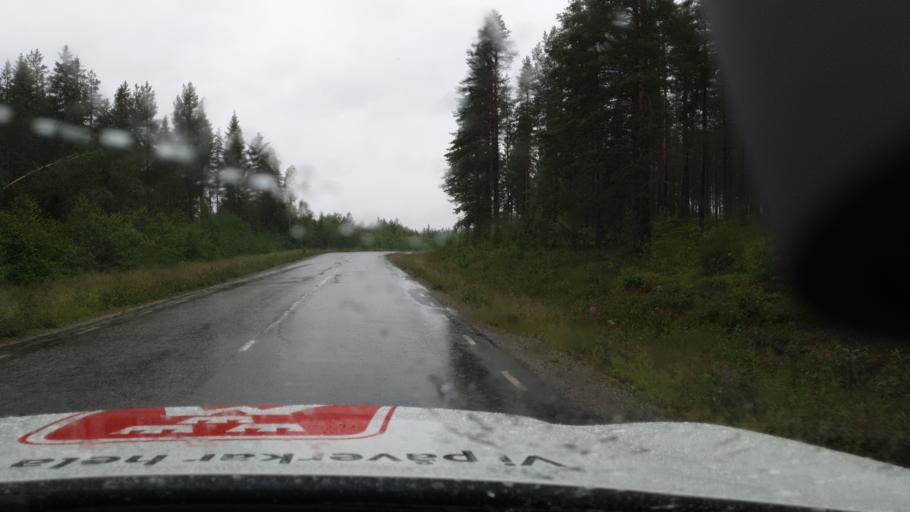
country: SE
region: Vaesterbotten
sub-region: Skelleftea Kommun
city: Langsele
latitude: 64.8382
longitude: 19.8866
